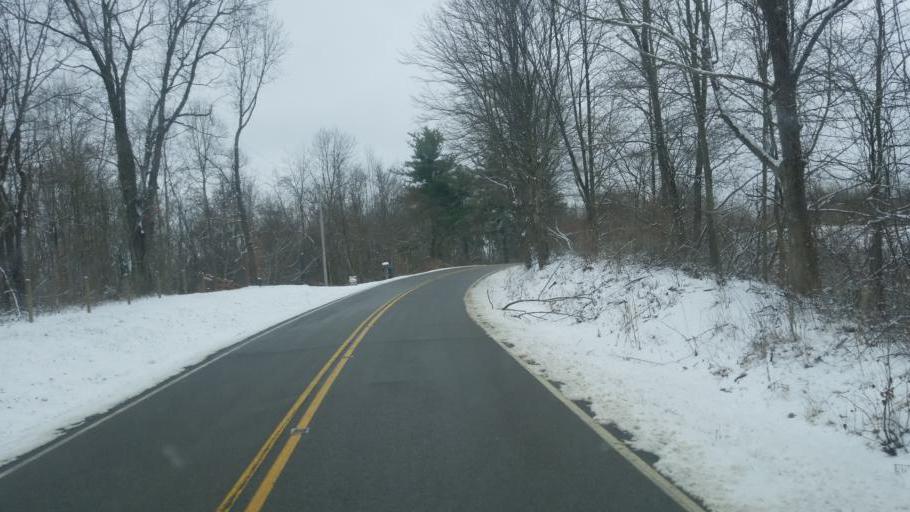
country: US
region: Ohio
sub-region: Knox County
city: Oak Hill
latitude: 40.3950
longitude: -82.1246
